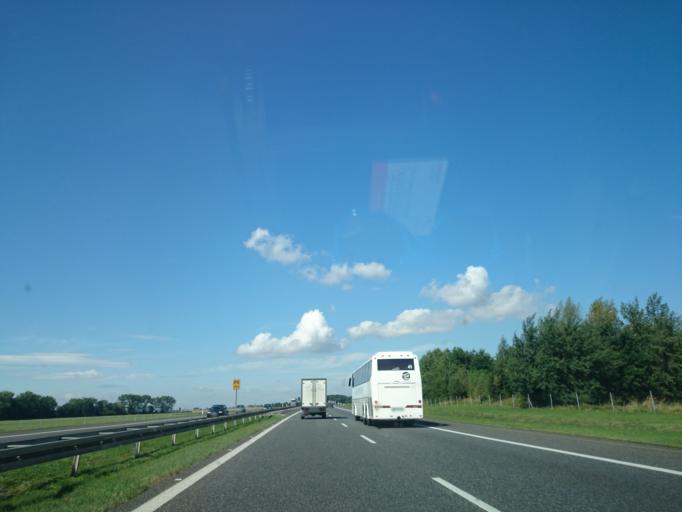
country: PL
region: Opole Voivodeship
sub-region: Powiat brzeski
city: Grodkow
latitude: 50.7698
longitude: 17.3888
